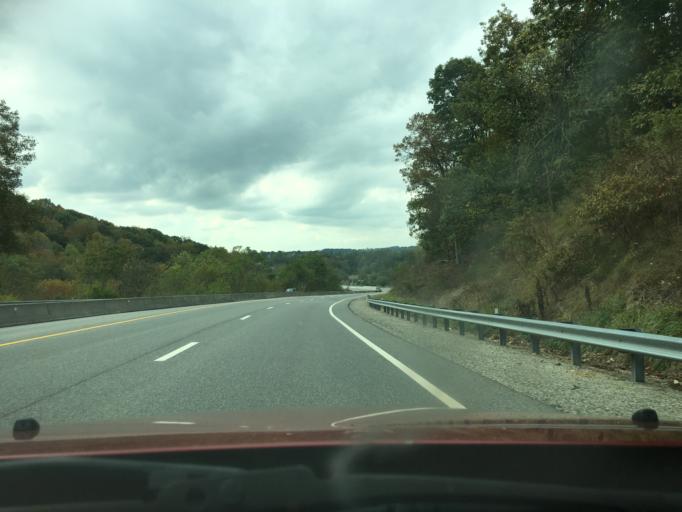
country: US
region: Virginia
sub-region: Pulaski County
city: Fairlawn
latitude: 37.1657
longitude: -80.5435
